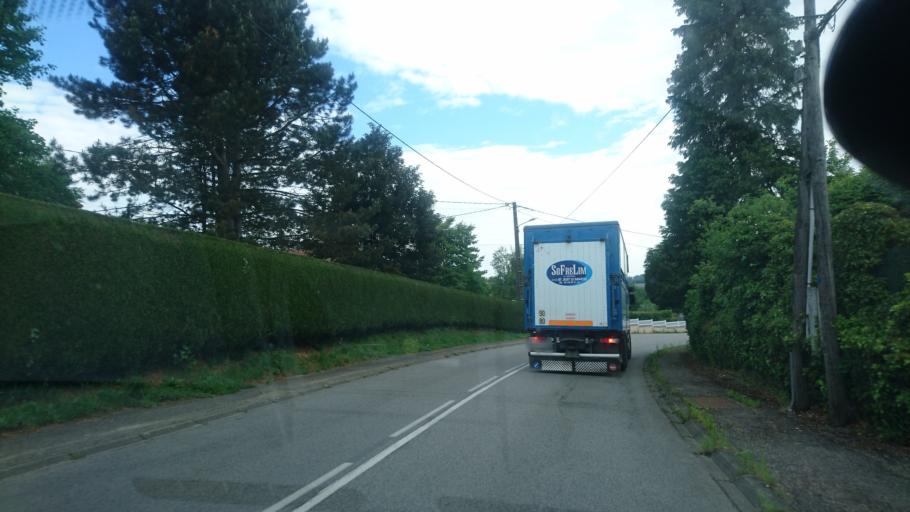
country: FR
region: Limousin
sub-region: Departement de la Haute-Vienne
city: Chateauneuf-la-Foret
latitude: 45.7086
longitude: 1.5964
